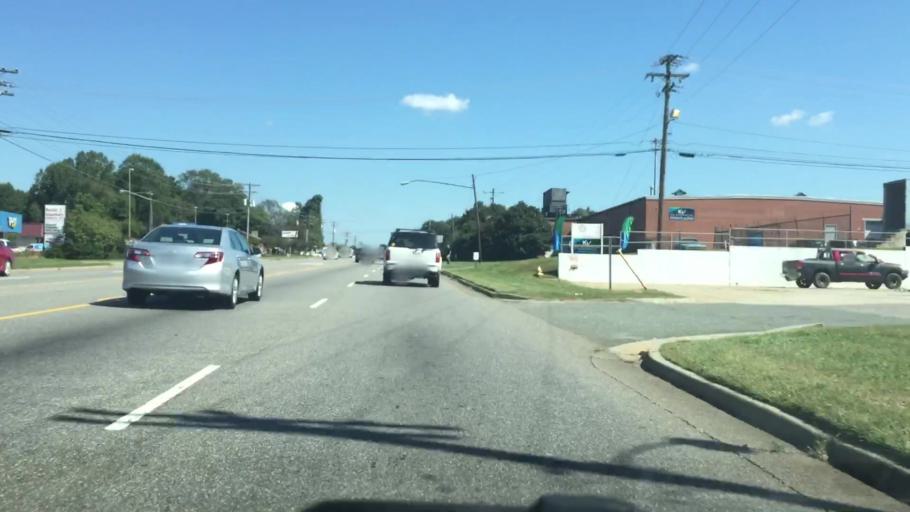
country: US
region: North Carolina
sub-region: Iredell County
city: Mooresville
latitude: 35.5922
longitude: -80.8215
